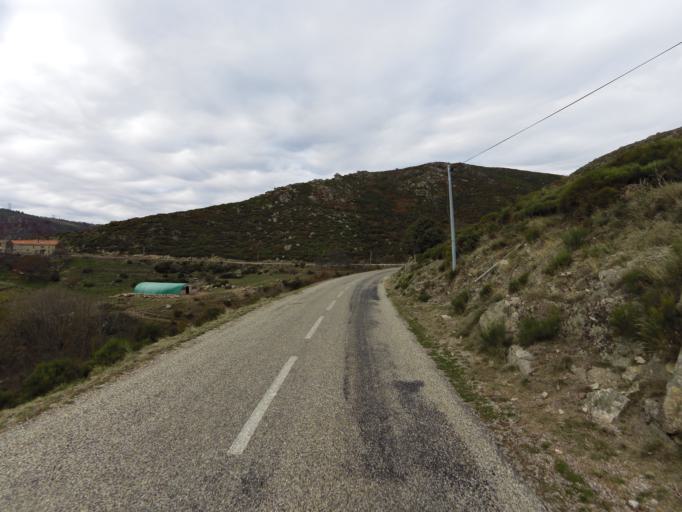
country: FR
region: Rhone-Alpes
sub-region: Departement de l'Ardeche
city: Les Vans
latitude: 44.5153
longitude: 4.0328
